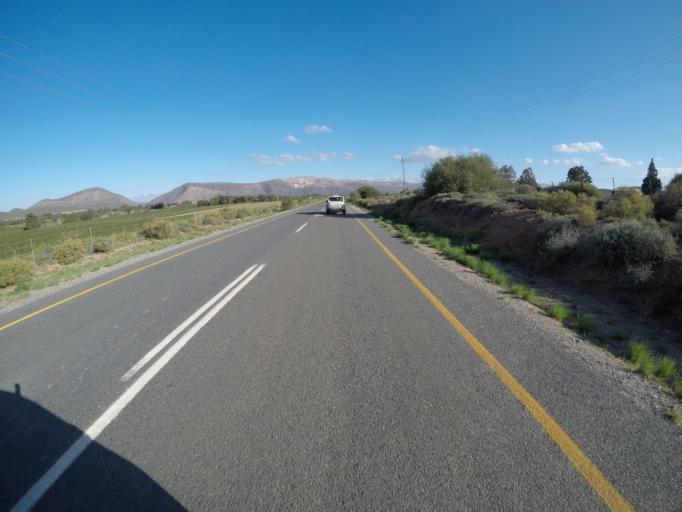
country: ZA
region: Western Cape
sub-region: Cape Winelands District Municipality
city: Ashton
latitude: -33.7978
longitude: 19.7810
